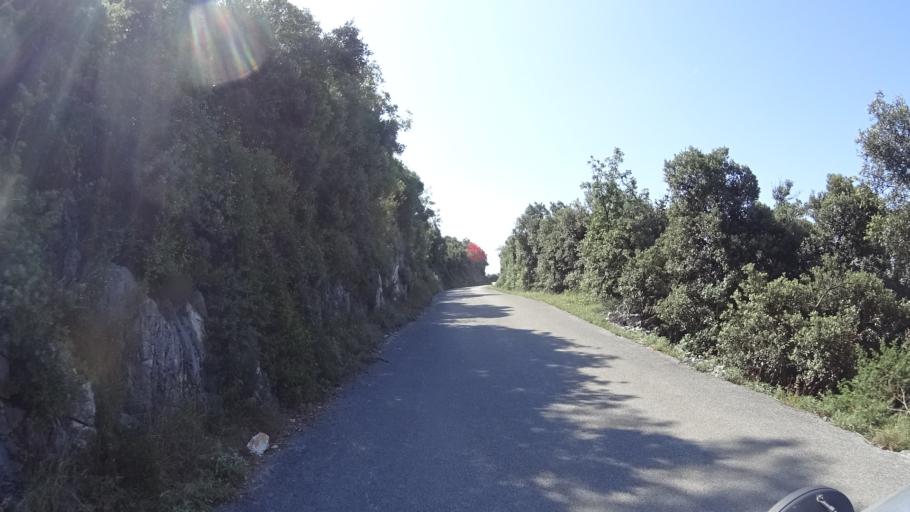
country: HR
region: Istarska
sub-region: Grad Labin
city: Rabac
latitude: 44.9703
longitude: 14.1443
